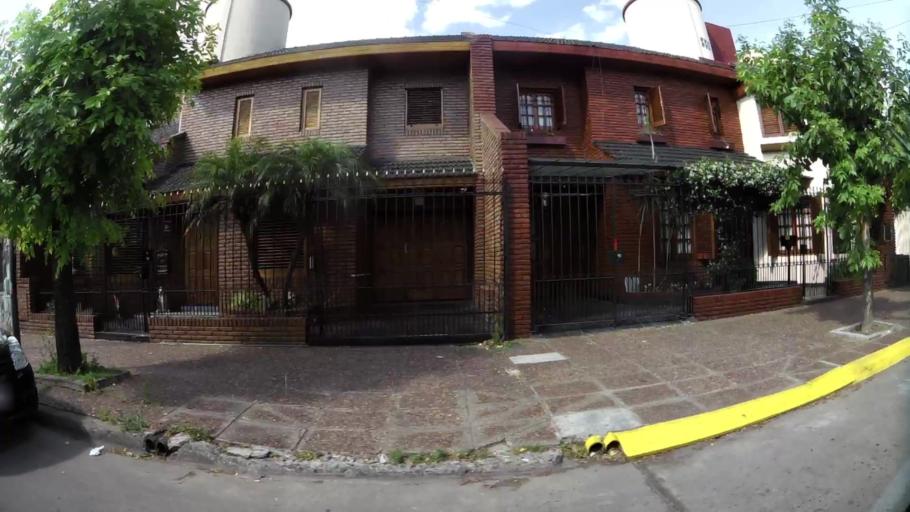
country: AR
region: Buenos Aires
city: San Justo
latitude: -34.6417
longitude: -58.5540
